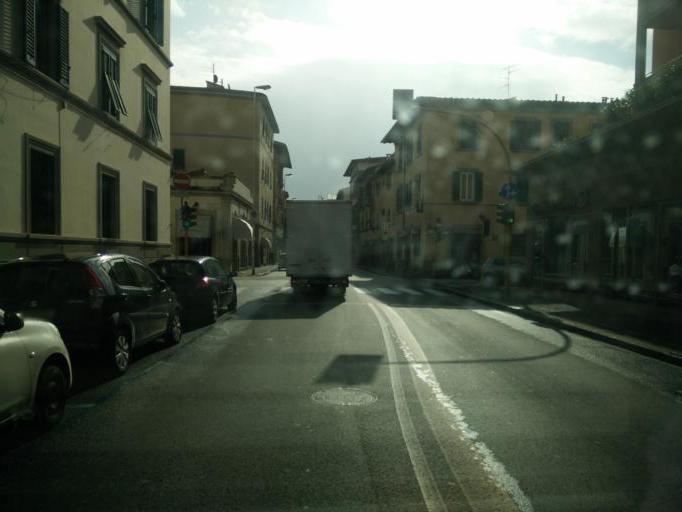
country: IT
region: Tuscany
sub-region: Province of Florence
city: Florence
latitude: 43.7841
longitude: 11.2319
